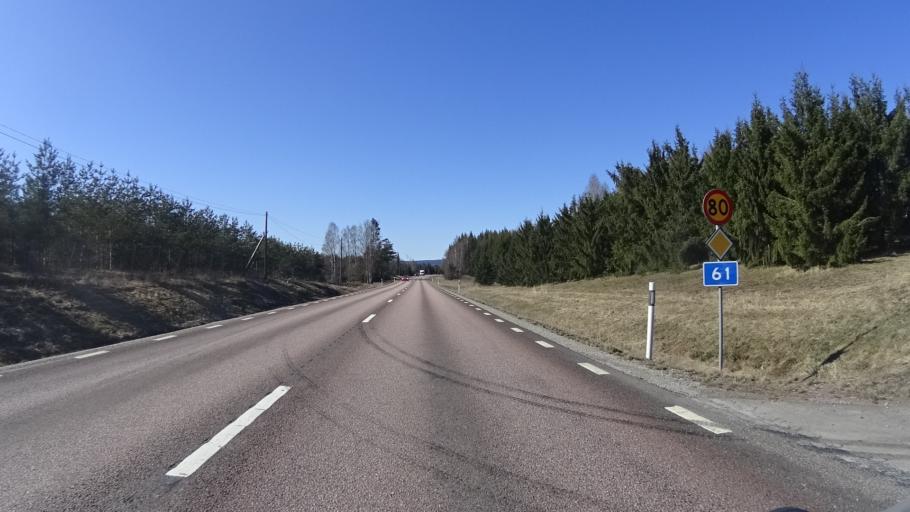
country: SE
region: Vaermland
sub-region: Sunne Kommun
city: Sunne
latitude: 59.6257
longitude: 12.9587
